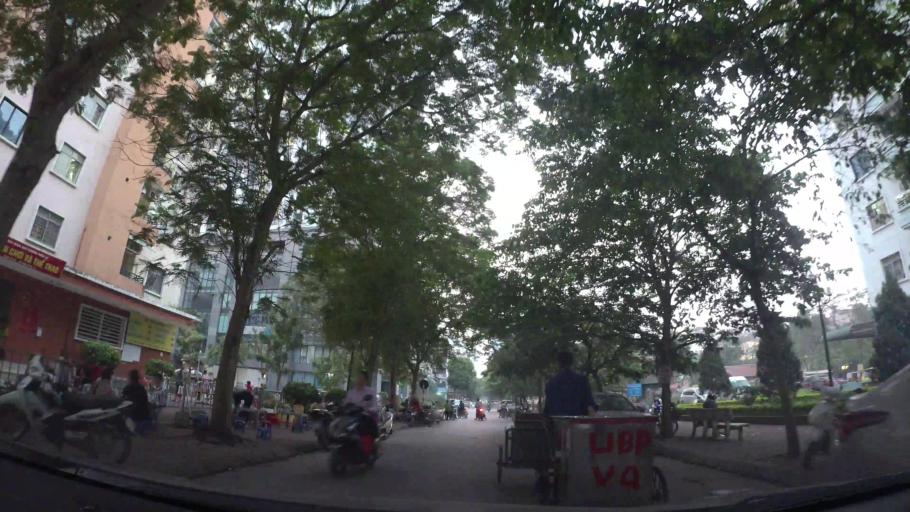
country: VN
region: Ha Noi
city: Ha Dong
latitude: 20.9743
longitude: 105.7886
